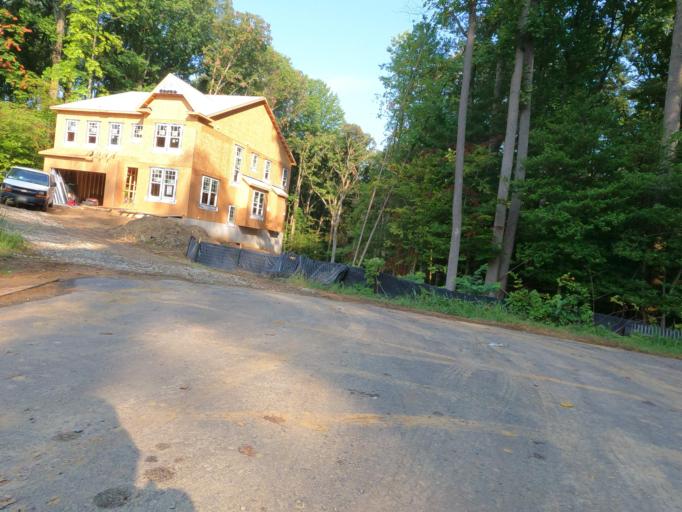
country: US
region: Maryland
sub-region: Anne Arundel County
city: Gambrills
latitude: 39.0665
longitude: -76.6582
